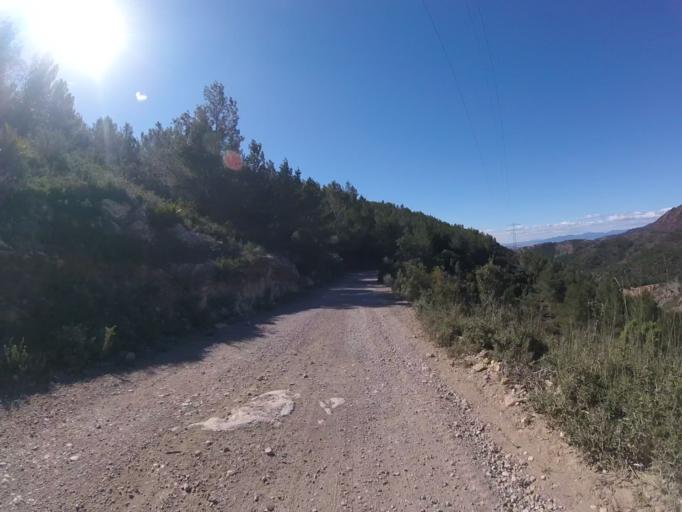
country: ES
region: Valencia
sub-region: Provincia de Castello
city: Benicassim
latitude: 40.0787
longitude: 0.0797
